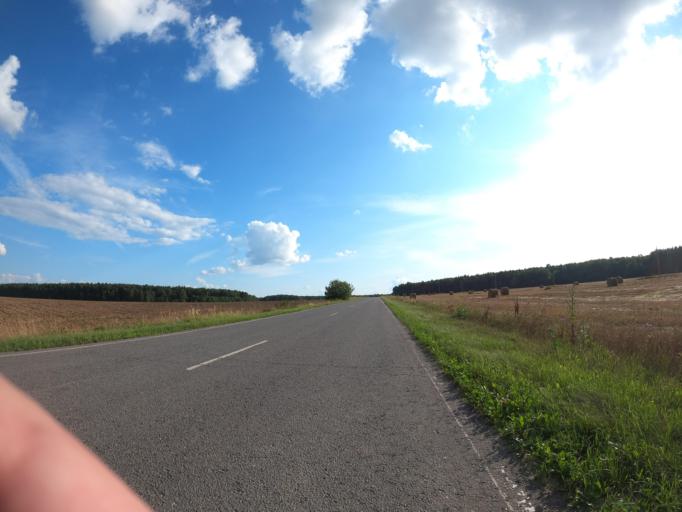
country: RU
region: Moskovskaya
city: Meshcherino
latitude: 55.1750
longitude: 38.4684
